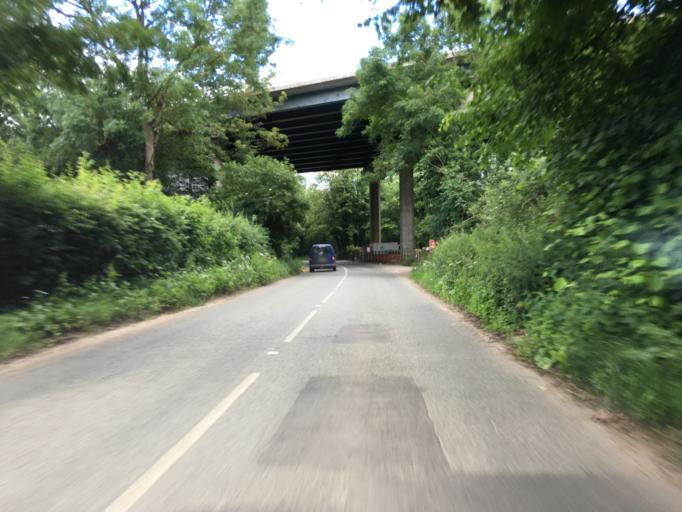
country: GB
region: England
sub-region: West Berkshire
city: Welford
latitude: 51.4501
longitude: -1.4049
